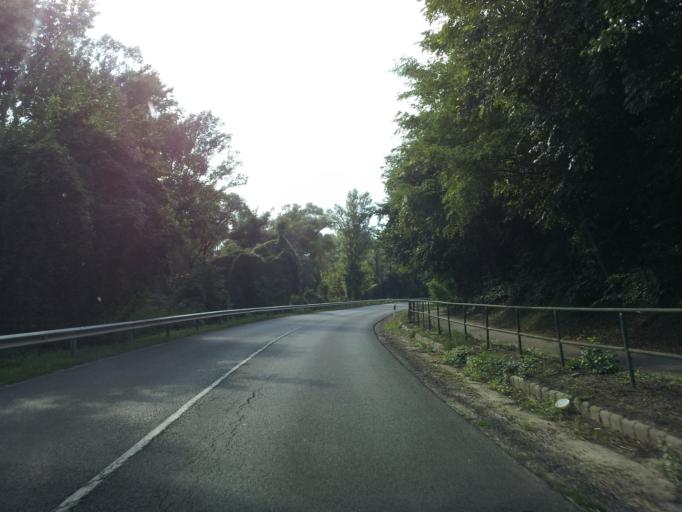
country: HU
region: Pest
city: Dunabogdany
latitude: 47.8137
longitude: 19.0772
